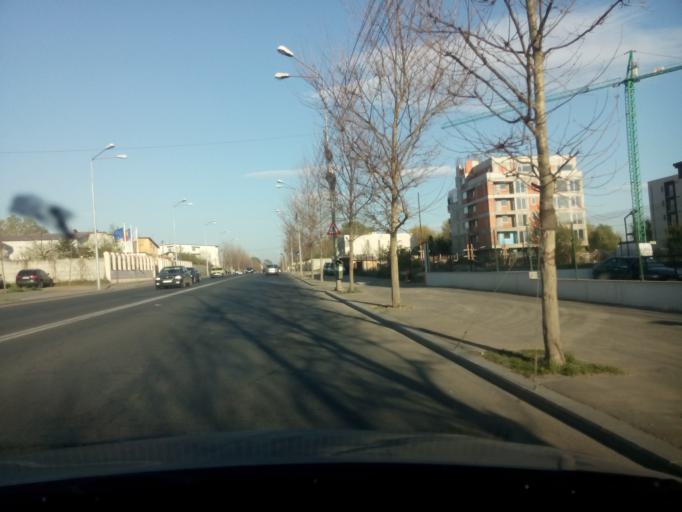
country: RO
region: Ilfov
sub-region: Comuna Otopeni
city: Otopeni
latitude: 44.5030
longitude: 26.0516
